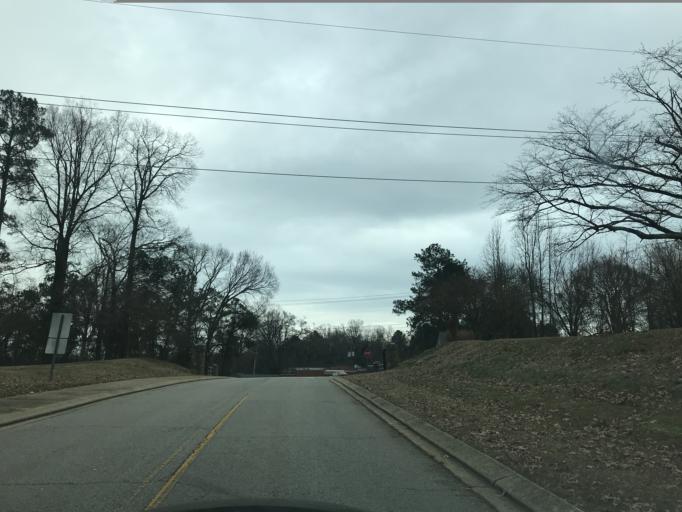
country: US
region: North Carolina
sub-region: Wake County
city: Raleigh
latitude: 35.7693
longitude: -78.6498
